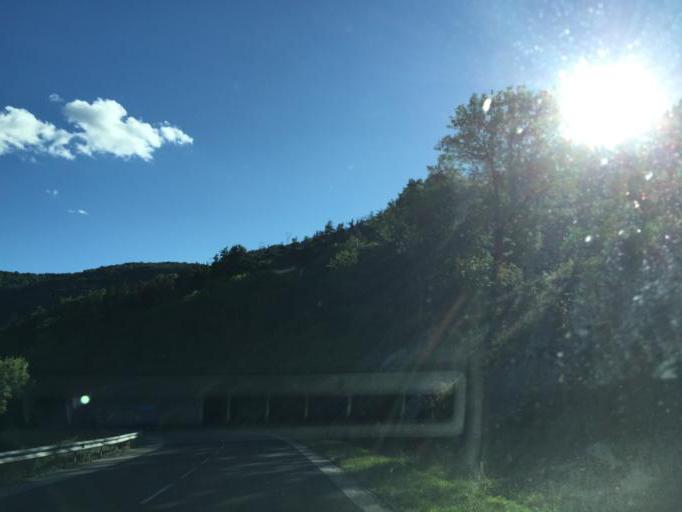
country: FR
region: Auvergne
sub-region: Departement de la Haute-Loire
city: Saugues
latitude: 44.9659
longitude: 3.6284
